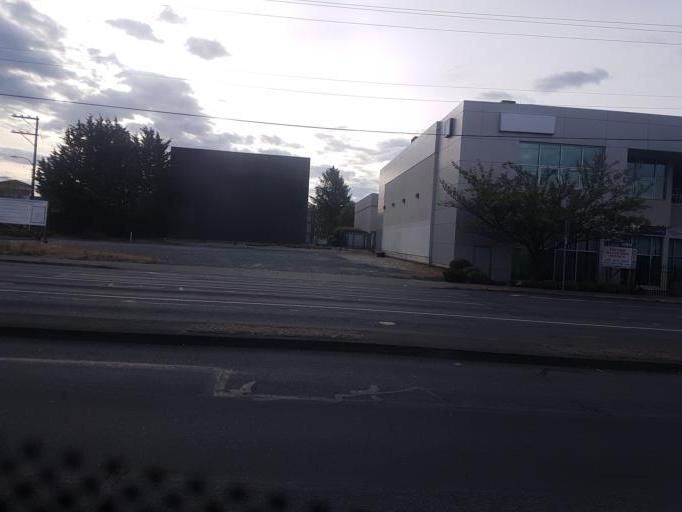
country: CA
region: British Columbia
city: Oak Bay
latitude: 48.4688
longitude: -123.3338
